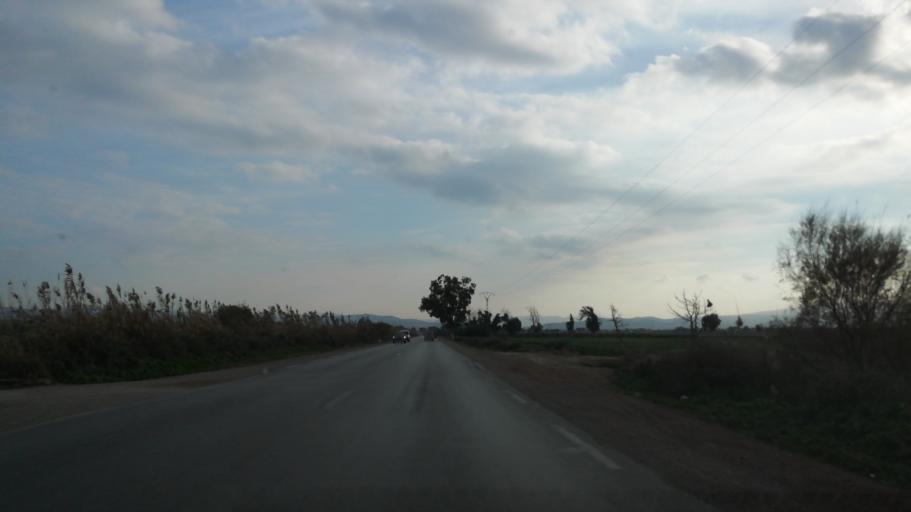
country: DZ
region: Mascara
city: Mascara
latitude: 35.6479
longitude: 0.0597
